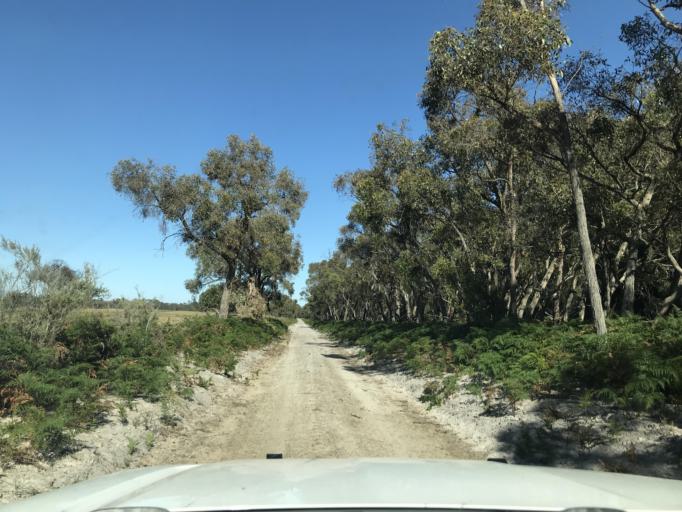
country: AU
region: South Australia
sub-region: Wattle Range
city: Penola
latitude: -37.0814
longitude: 141.3928
